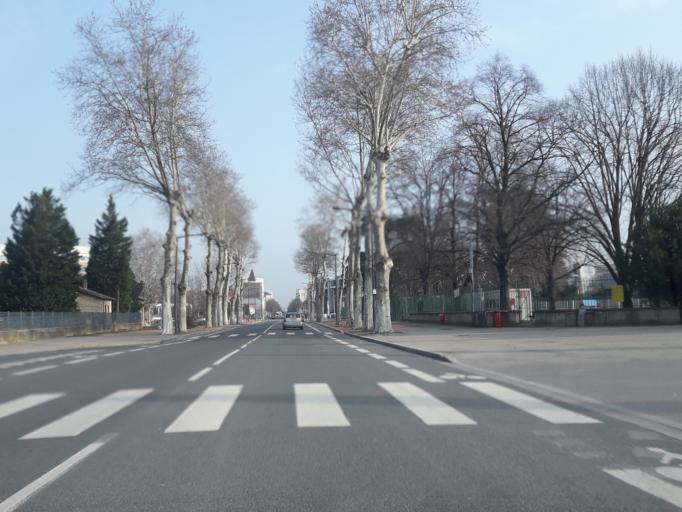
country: FR
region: Rhone-Alpes
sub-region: Departement du Rhone
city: La Mulatiere
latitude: 45.7245
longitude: 4.8296
